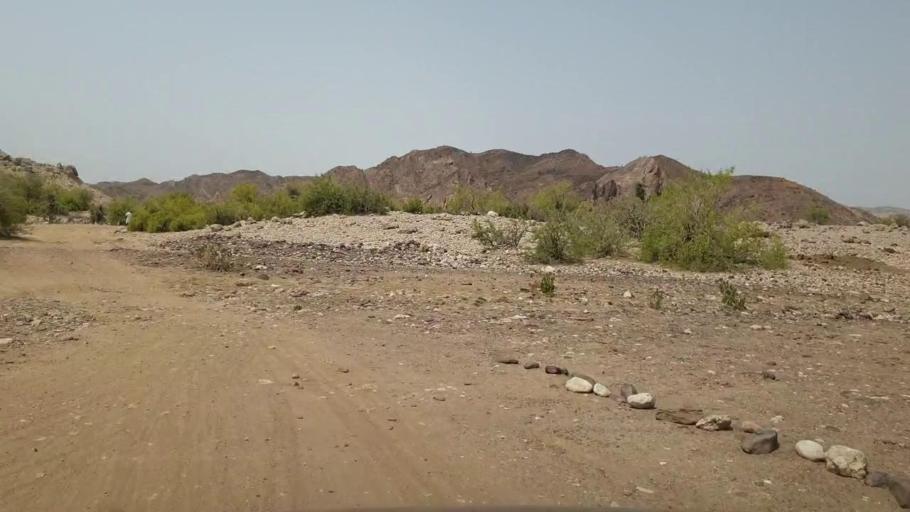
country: PK
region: Sindh
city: Sann
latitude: 25.8845
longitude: 67.9265
